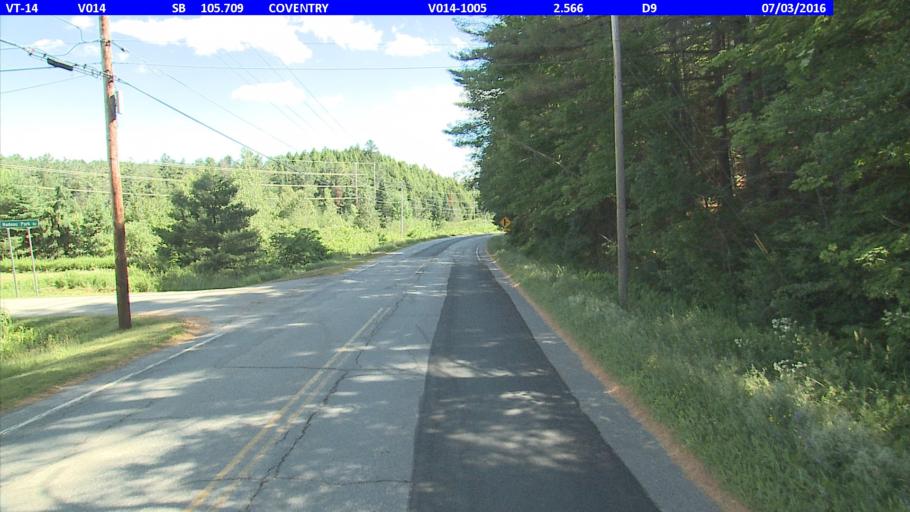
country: US
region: Vermont
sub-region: Orleans County
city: Newport
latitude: 44.9000
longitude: -72.2577
